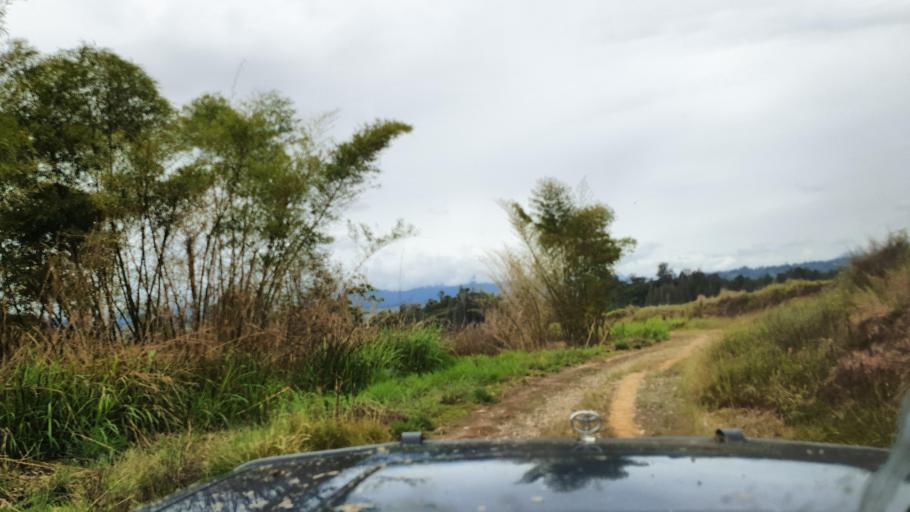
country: PG
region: Jiwaka
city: Minj
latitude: -5.9276
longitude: 144.7466
